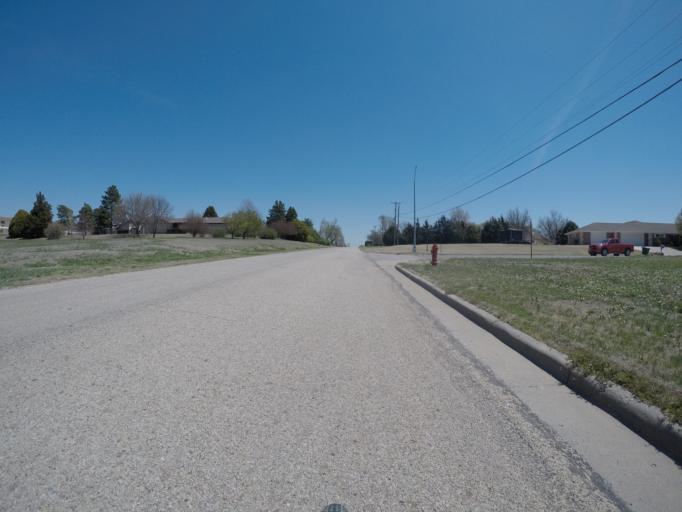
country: US
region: Kansas
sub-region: Pratt County
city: Pratt
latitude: 37.6420
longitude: -98.7569
